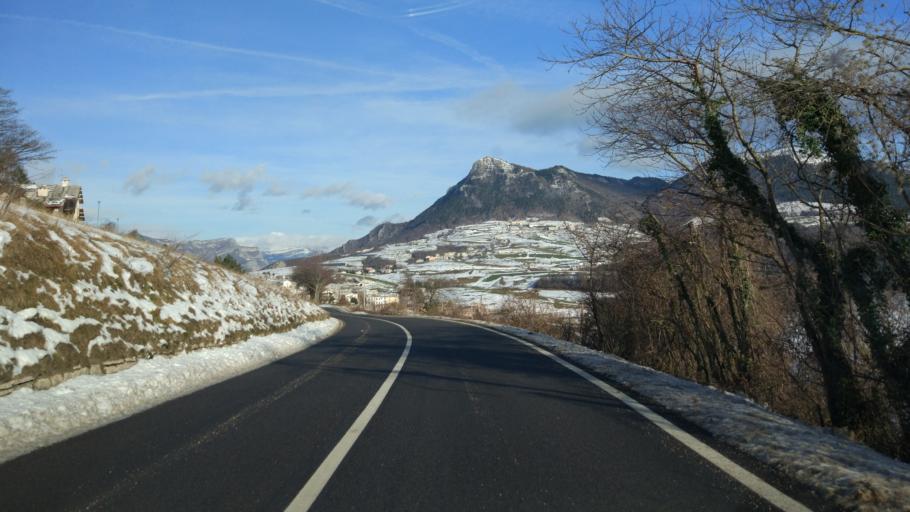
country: IT
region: Veneto
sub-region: Provincia di Verona
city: Sant'Anna d'Alfaedo
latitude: 45.6384
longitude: 10.9406
